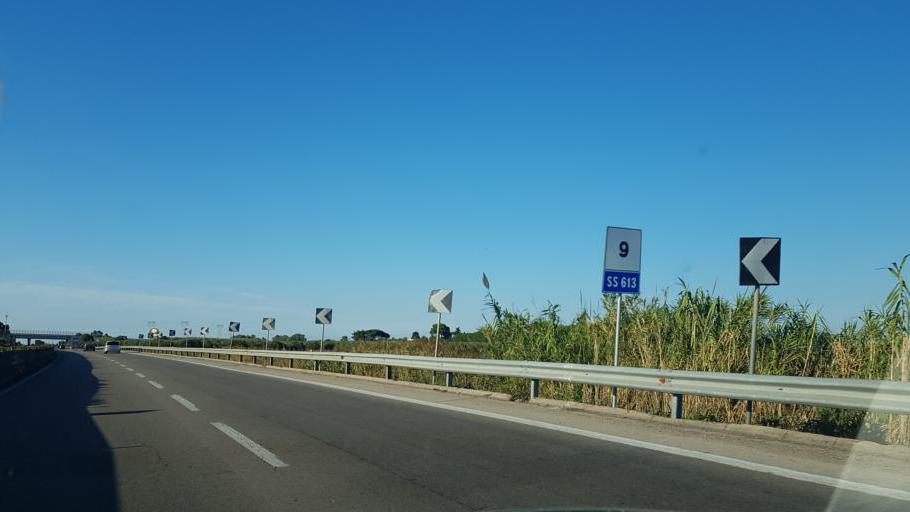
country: IT
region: Apulia
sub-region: Provincia di Brindisi
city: Tuturano
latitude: 40.5495
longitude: 17.9977
